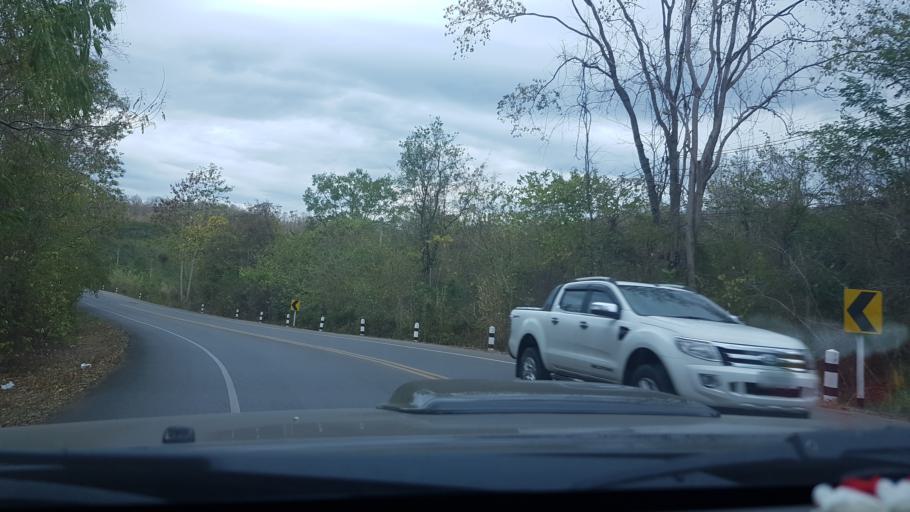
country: TH
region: Phetchabun
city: Phetchabun
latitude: 16.5336
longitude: 101.1080
